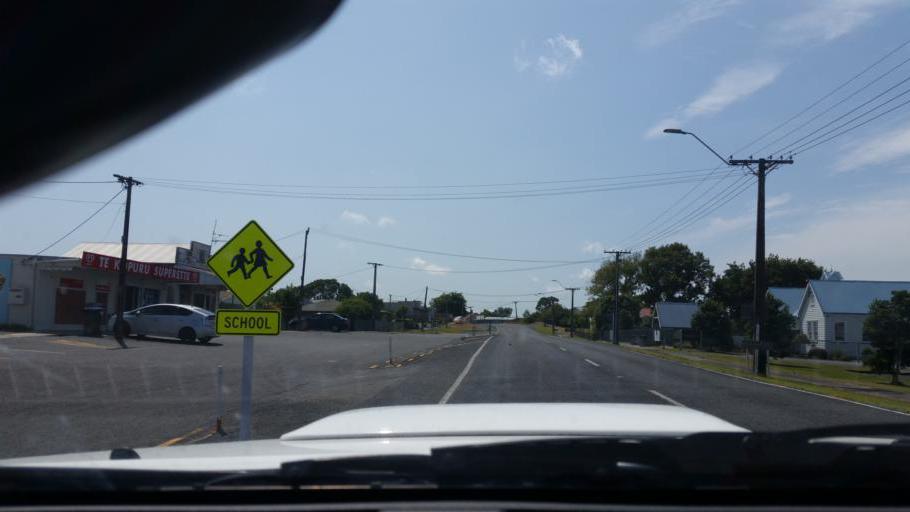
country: NZ
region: Northland
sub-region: Kaipara District
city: Dargaville
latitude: -36.0306
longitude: 173.9231
